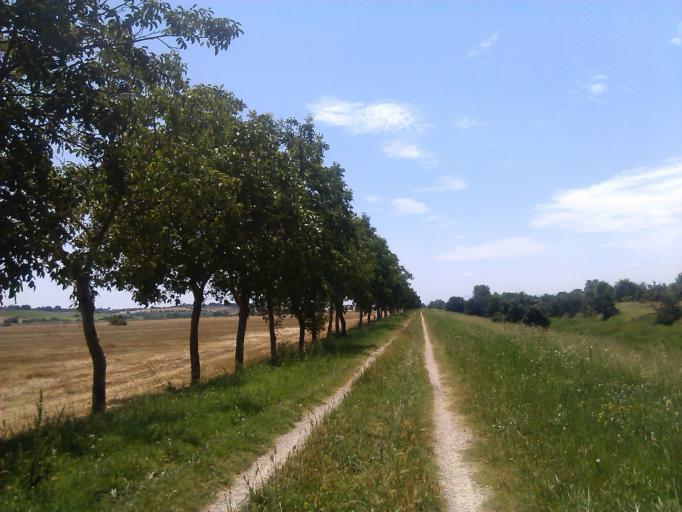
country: IT
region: Tuscany
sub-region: Province of Arezzo
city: Cesa
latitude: 43.3134
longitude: 11.8380
